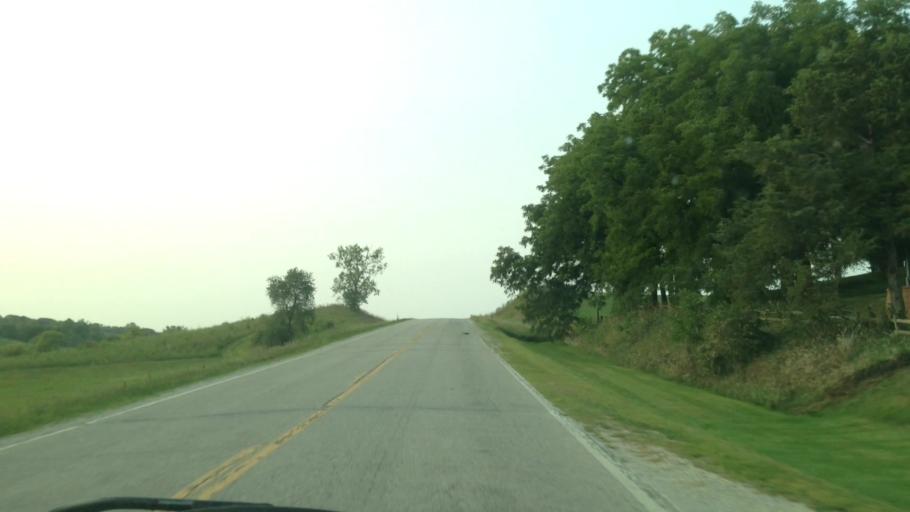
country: US
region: Iowa
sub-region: Iowa County
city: Marengo
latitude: 41.8776
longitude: -92.0890
